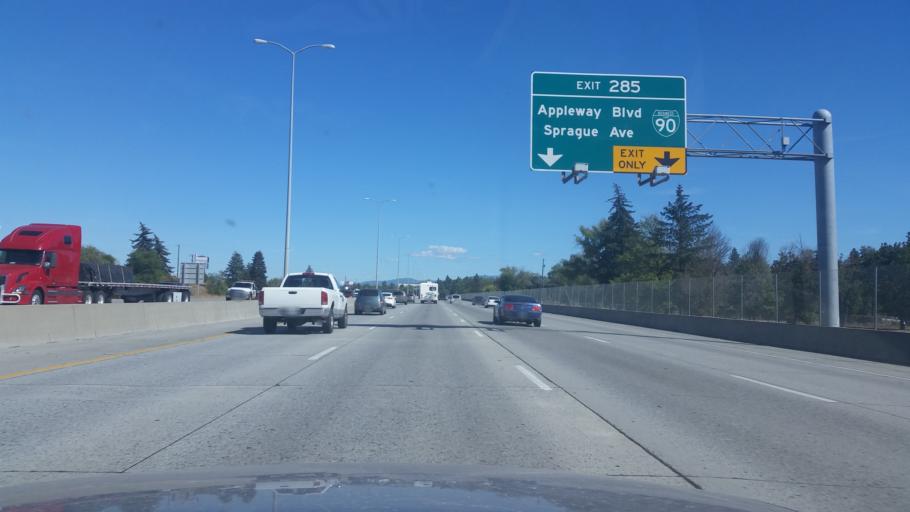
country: US
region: Washington
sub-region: Spokane County
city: Millwood
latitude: 47.6538
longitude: -117.3395
